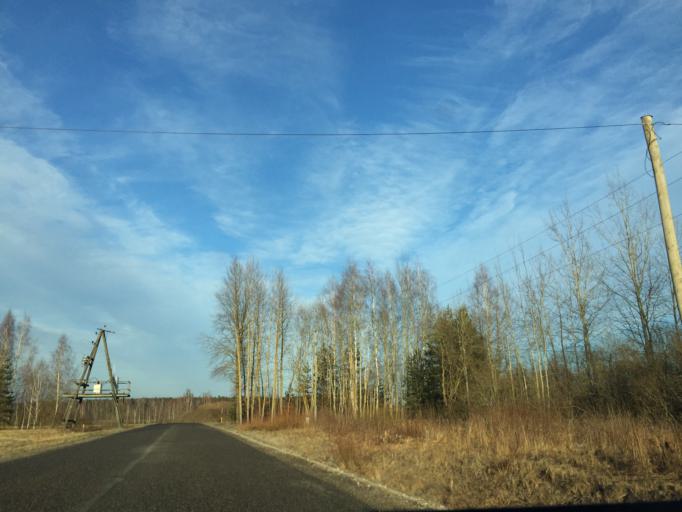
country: LV
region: Kekava
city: Kekava
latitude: 56.8121
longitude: 24.1819
